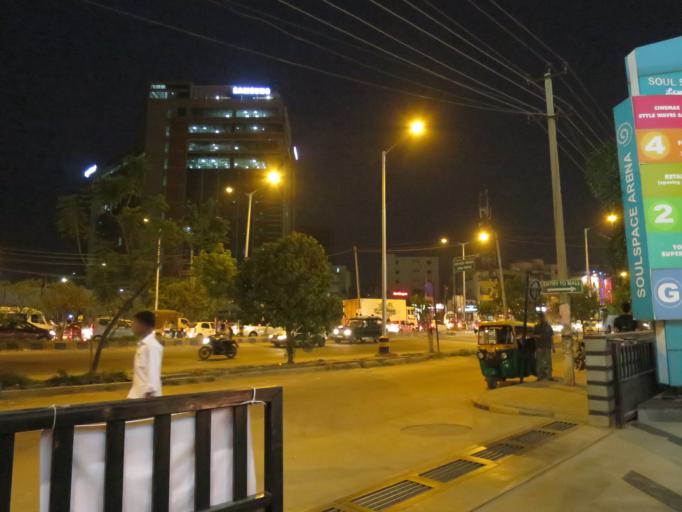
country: IN
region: Karnataka
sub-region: Bangalore Urban
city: Bangalore
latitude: 12.9798
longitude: 77.6942
